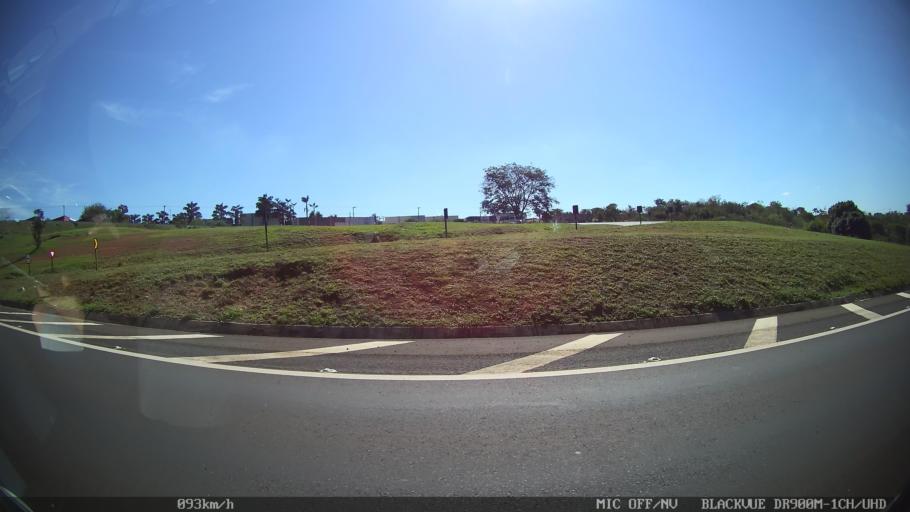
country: BR
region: Sao Paulo
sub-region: Franca
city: Franca
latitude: -20.5572
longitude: -47.4390
